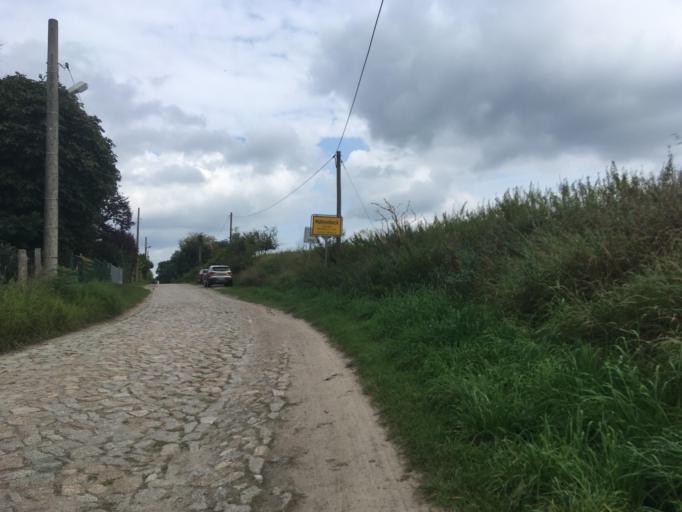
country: DE
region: Brandenburg
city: Glienicke
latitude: 52.6715
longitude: 13.3675
